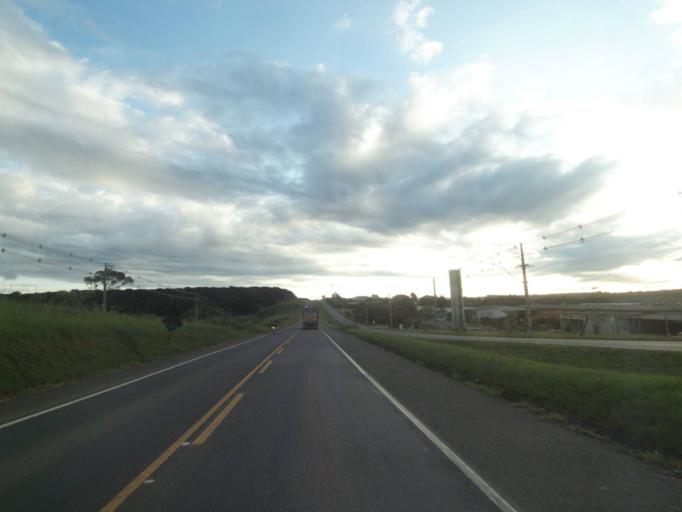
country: BR
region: Parana
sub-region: Telemaco Borba
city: Telemaco Borba
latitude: -24.3699
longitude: -50.6607
